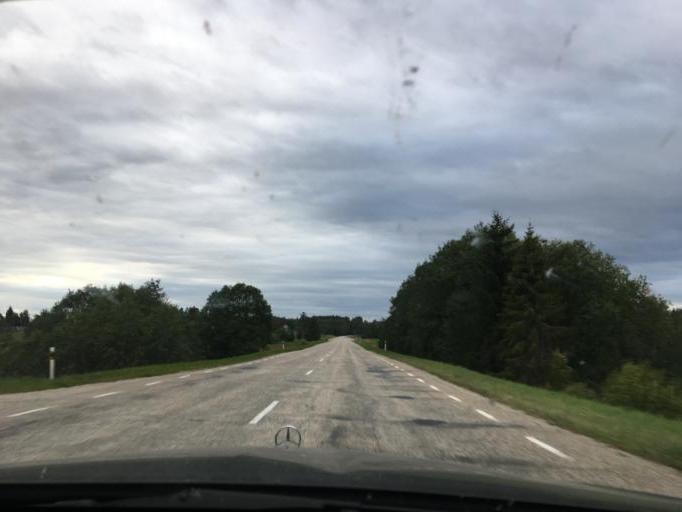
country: LV
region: Aluksnes Rajons
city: Aluksne
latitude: 57.6112
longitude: 27.2579
